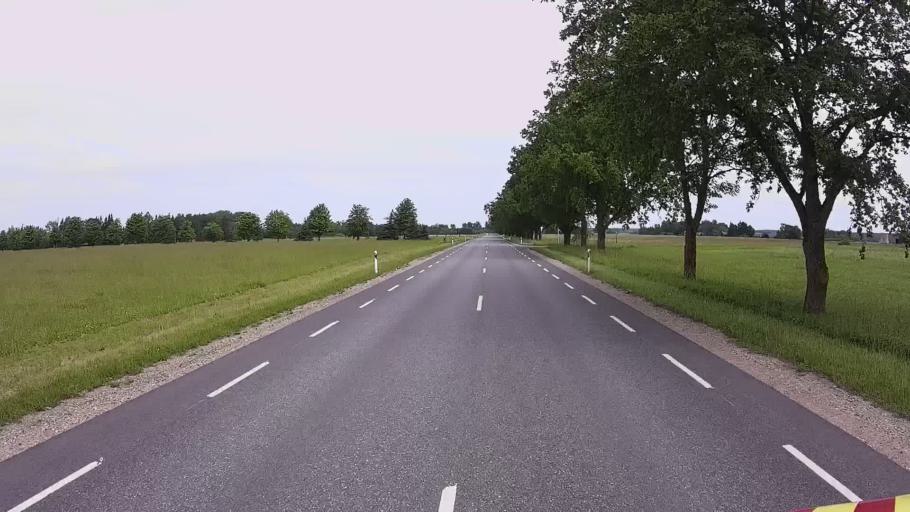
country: EE
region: Viljandimaa
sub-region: Karksi vald
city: Karksi-Nuia
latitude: 58.1245
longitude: 25.5826
